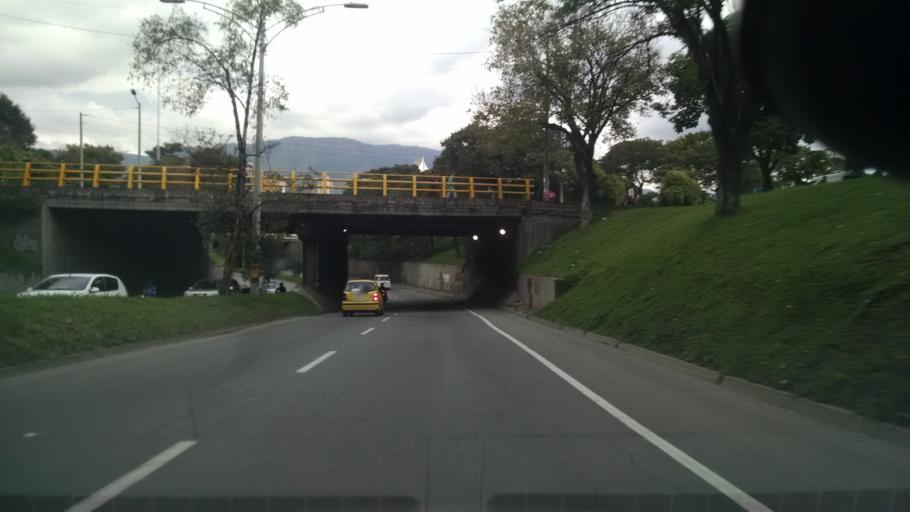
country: CO
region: Antioquia
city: Medellin
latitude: 6.2586
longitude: -75.5721
